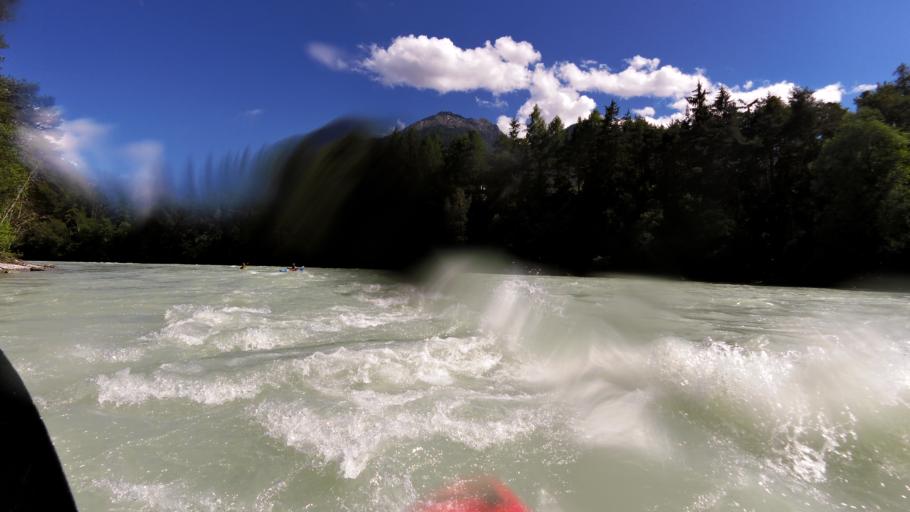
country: AT
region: Tyrol
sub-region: Politischer Bezirk Imst
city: Roppen
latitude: 47.2264
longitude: 10.8242
